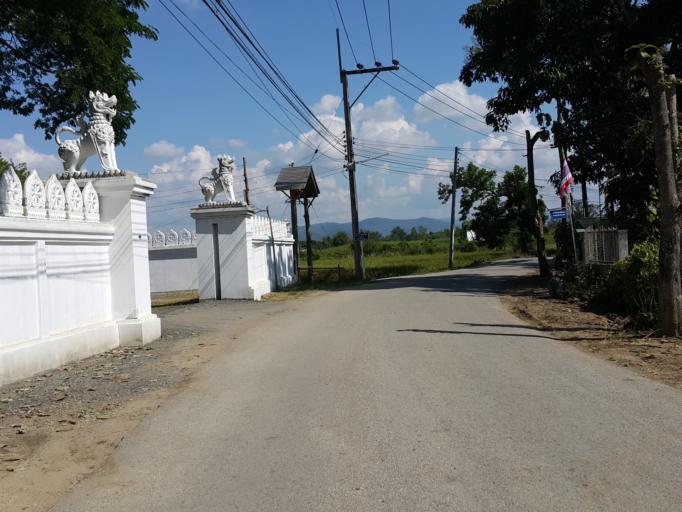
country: TH
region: Chiang Mai
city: San Kamphaeng
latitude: 18.7783
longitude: 99.1229
